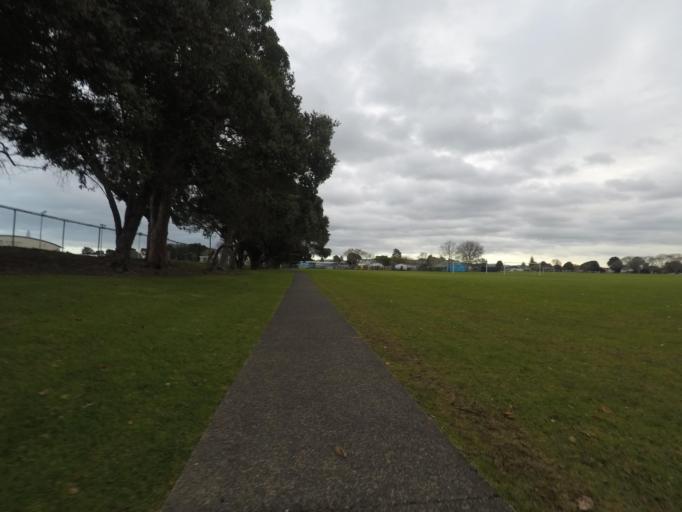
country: NZ
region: Auckland
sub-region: Auckland
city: Rosebank
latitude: -36.8880
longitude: 174.6890
